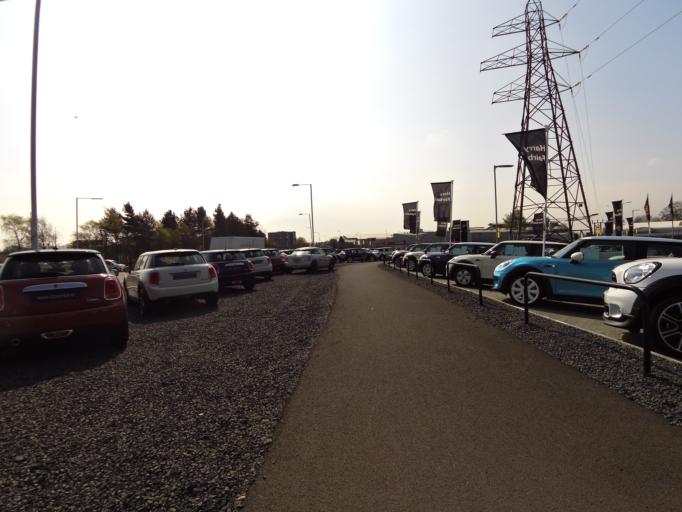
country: GB
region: Scotland
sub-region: Fife
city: Kirkcaldy
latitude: 56.1351
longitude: -3.1488
